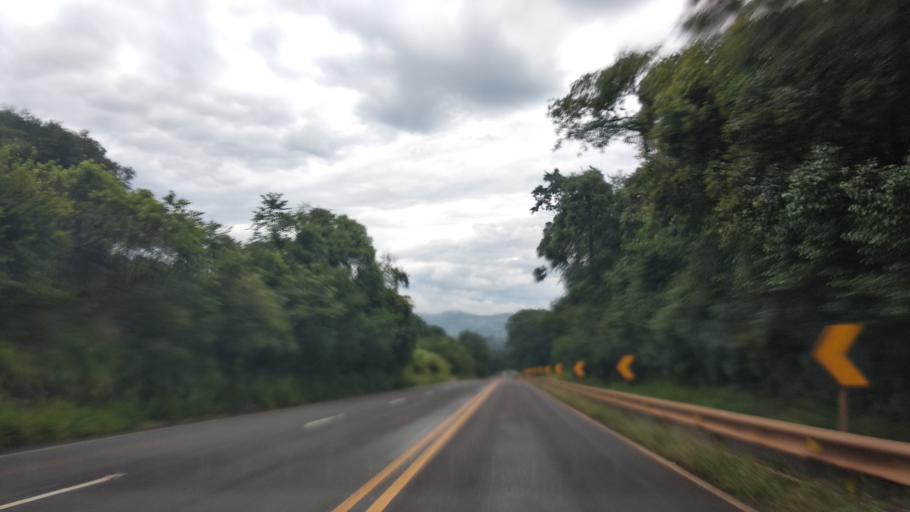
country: BR
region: Santa Catarina
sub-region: Videira
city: Videira
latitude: -27.0809
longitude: -51.2367
